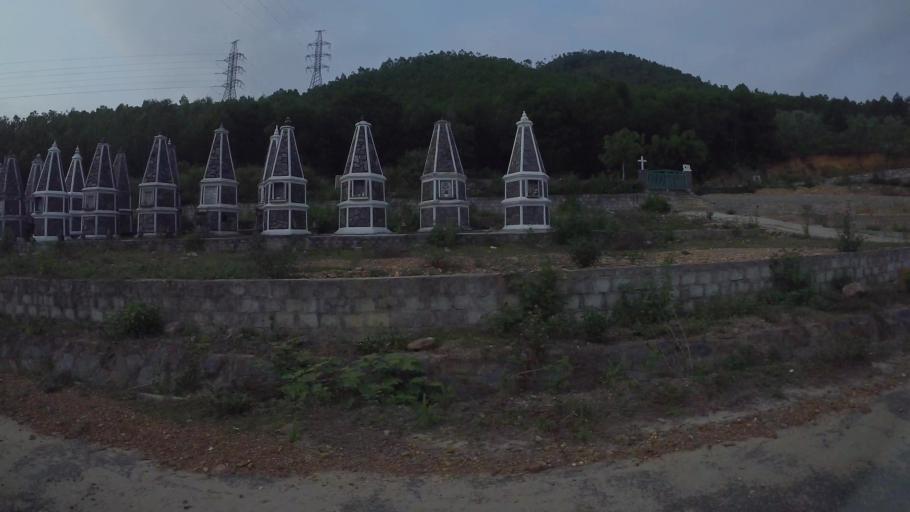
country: VN
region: Da Nang
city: Lien Chieu
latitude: 16.0632
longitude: 108.1108
